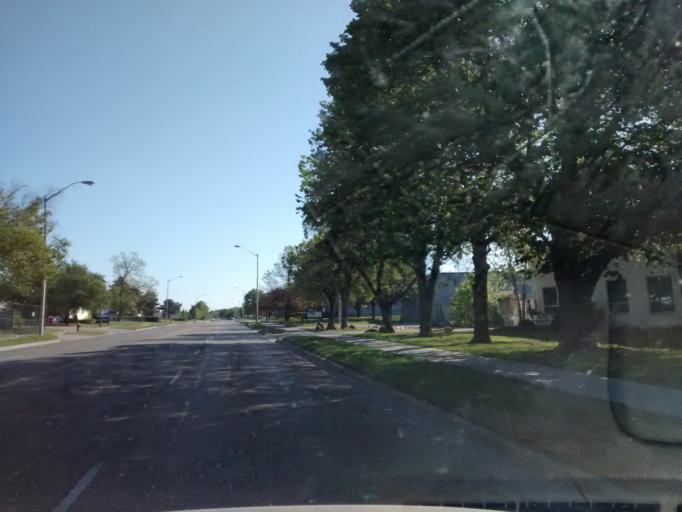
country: CA
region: Ontario
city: Burlington
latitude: 43.3645
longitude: -79.8030
